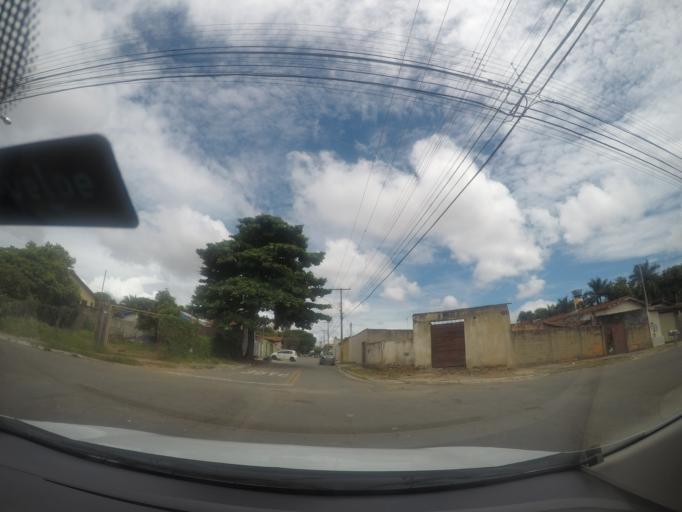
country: BR
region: Goias
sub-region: Goiania
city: Goiania
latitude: -16.6652
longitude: -49.3007
